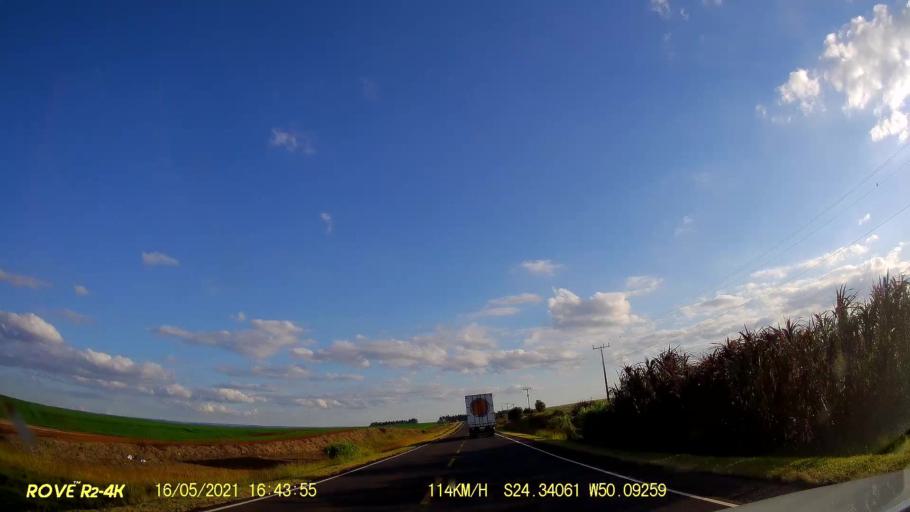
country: BR
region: Parana
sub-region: Pirai Do Sul
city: Pirai do Sul
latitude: -24.3408
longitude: -50.0925
